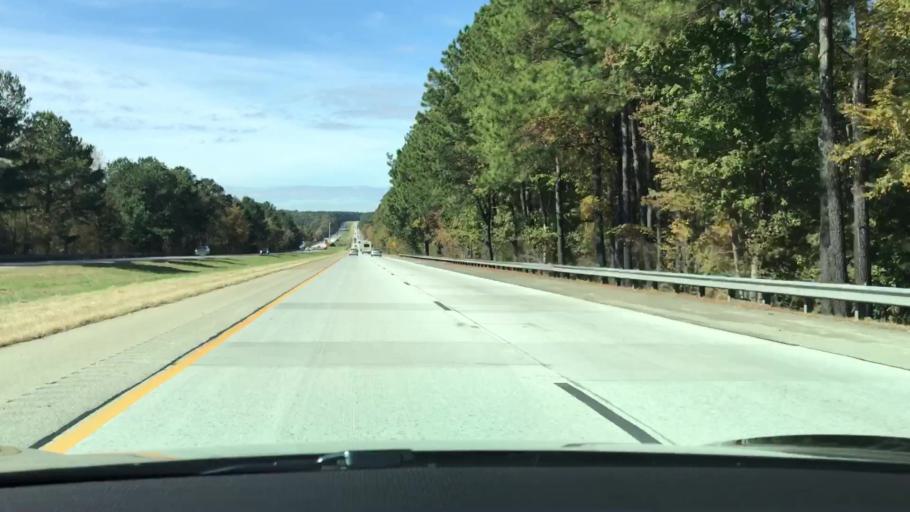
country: US
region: Georgia
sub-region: Greene County
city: Greensboro
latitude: 33.5349
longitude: -83.2623
